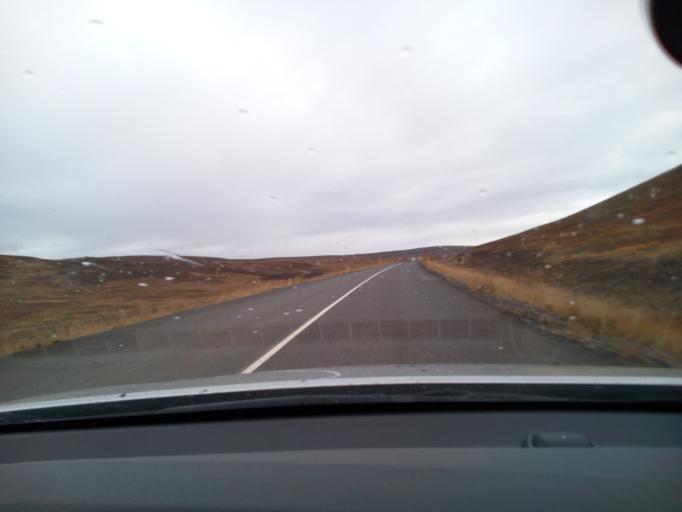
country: IS
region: Northeast
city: Laugar
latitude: 65.7963
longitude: -17.2419
